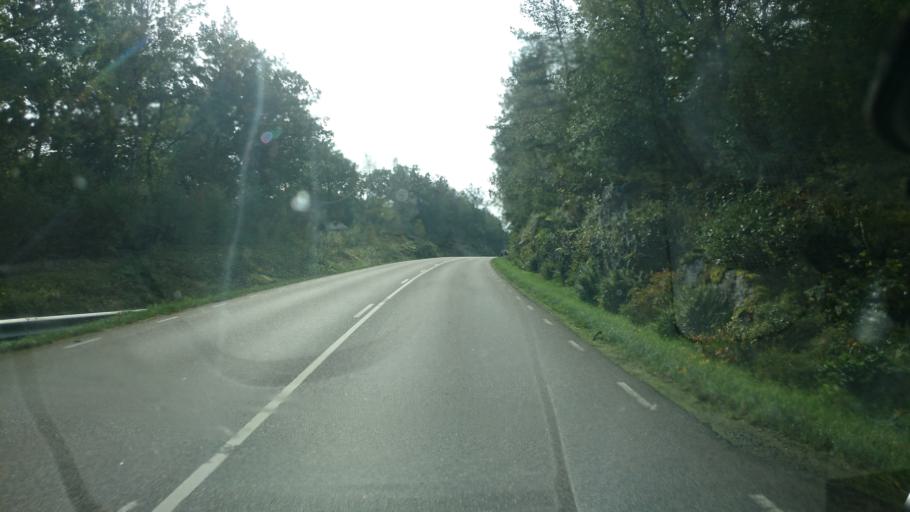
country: SE
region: Vaestra Goetaland
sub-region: Alingsas Kommun
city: Sollebrunn
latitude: 58.0512
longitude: 12.4682
